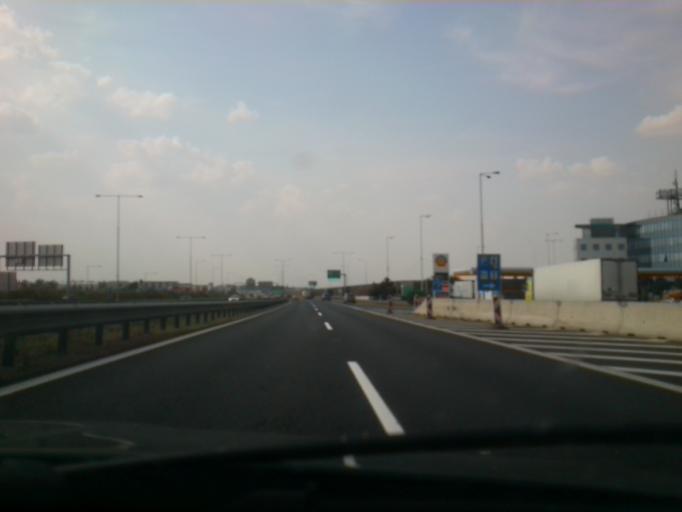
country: CZ
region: Central Bohemia
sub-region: Okres Praha-Vychod
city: Ricany
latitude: 49.9832
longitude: 14.6035
